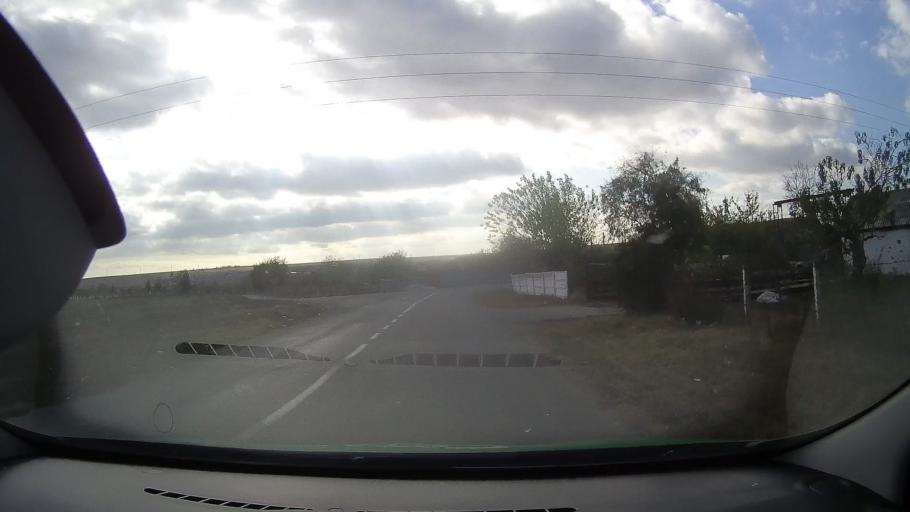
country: RO
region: Constanta
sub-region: Comuna Sacele
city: Sacele
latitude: 44.4903
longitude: 28.6528
